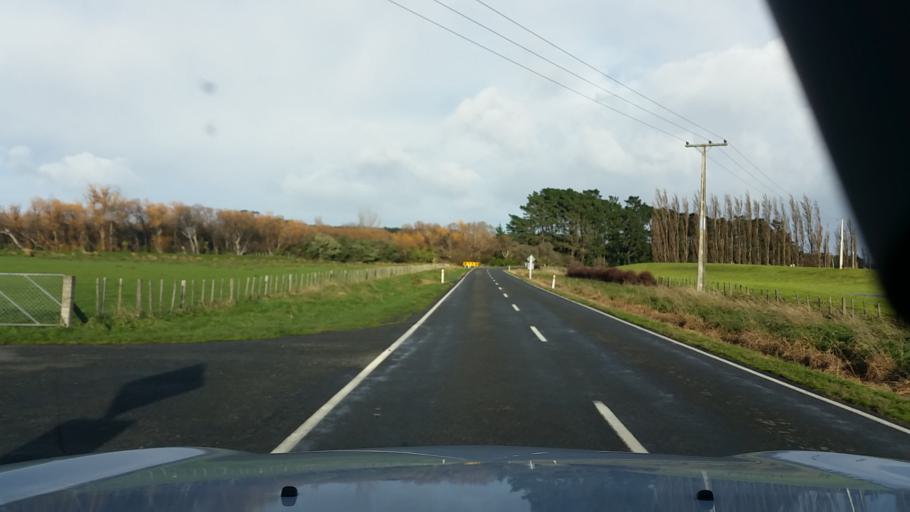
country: NZ
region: Wellington
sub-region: Upper Hutt City
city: Upper Hutt
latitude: -41.3675
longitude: 175.1865
